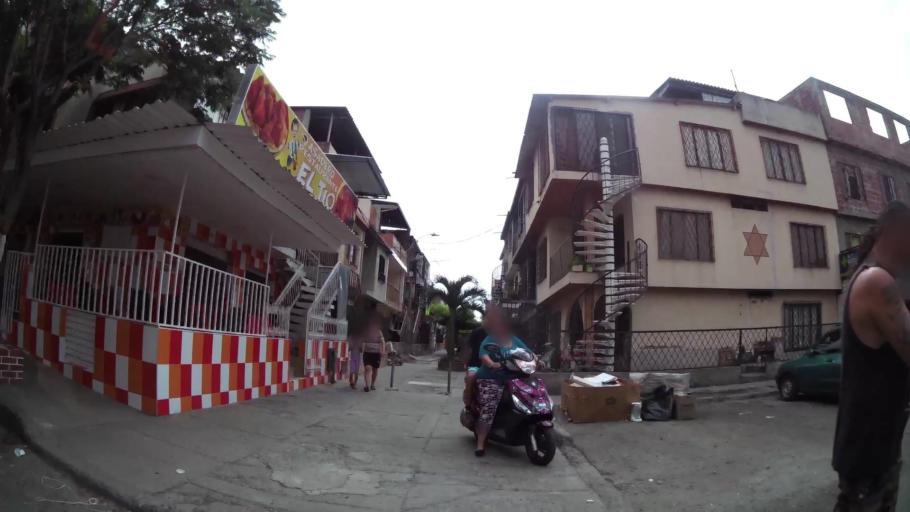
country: CO
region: Valle del Cauca
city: Cali
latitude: 3.4950
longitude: -76.4874
